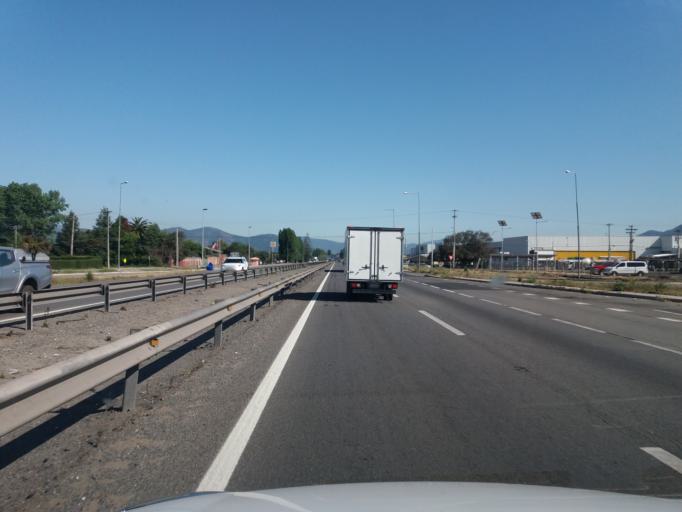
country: CL
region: Valparaiso
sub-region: Provincia de Quillota
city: Hacienda La Calera
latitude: -32.8013
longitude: -71.1555
